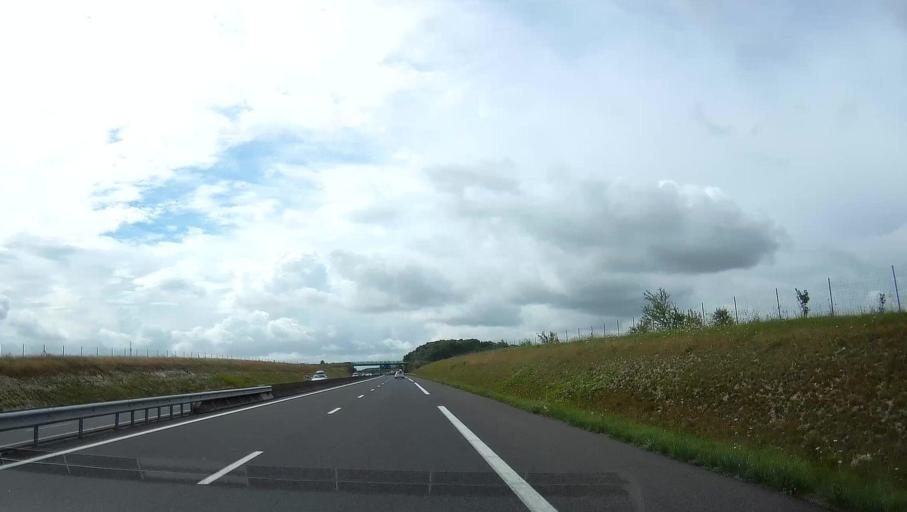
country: FR
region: Champagne-Ardenne
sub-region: Departement de la Marne
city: Fagnieres
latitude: 48.9157
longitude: 4.2832
